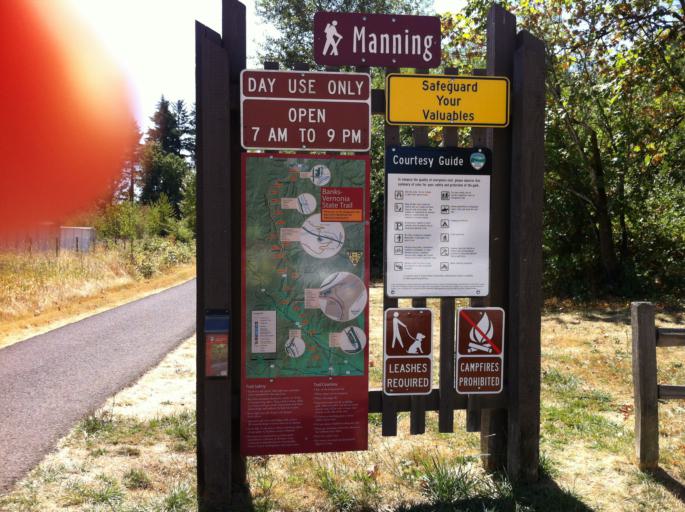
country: US
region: Oregon
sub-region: Washington County
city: Banks
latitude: 45.6648
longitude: -123.1634
